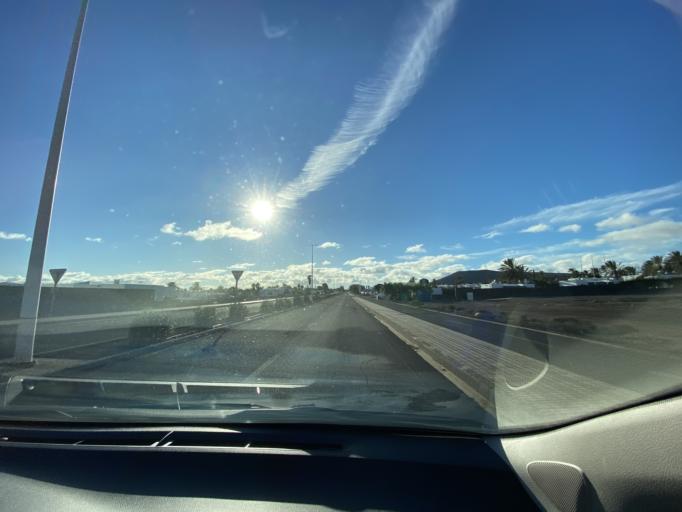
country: ES
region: Canary Islands
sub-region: Provincia de Las Palmas
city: Playa Blanca
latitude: 28.8682
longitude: -13.8329
